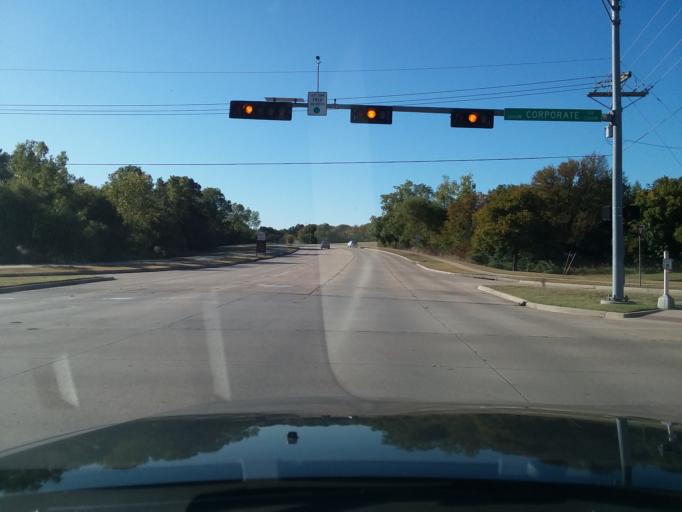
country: US
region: Texas
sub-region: Denton County
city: Lewisville
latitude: 33.0207
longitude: -97.0281
